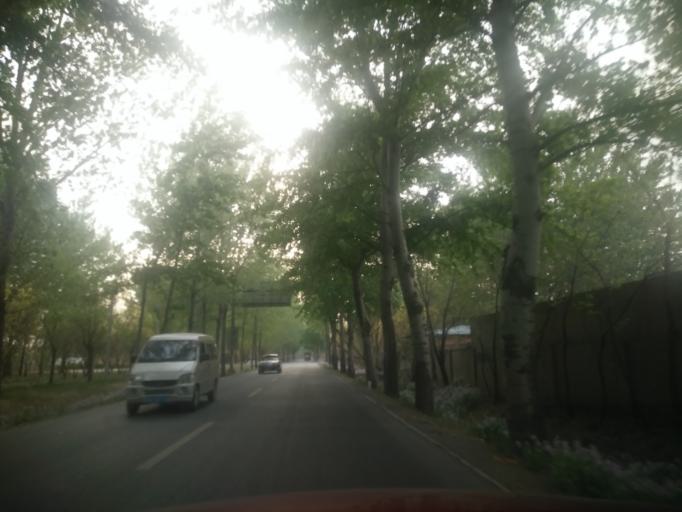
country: CN
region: Beijing
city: Qingyundian
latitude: 39.6771
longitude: 116.4945
